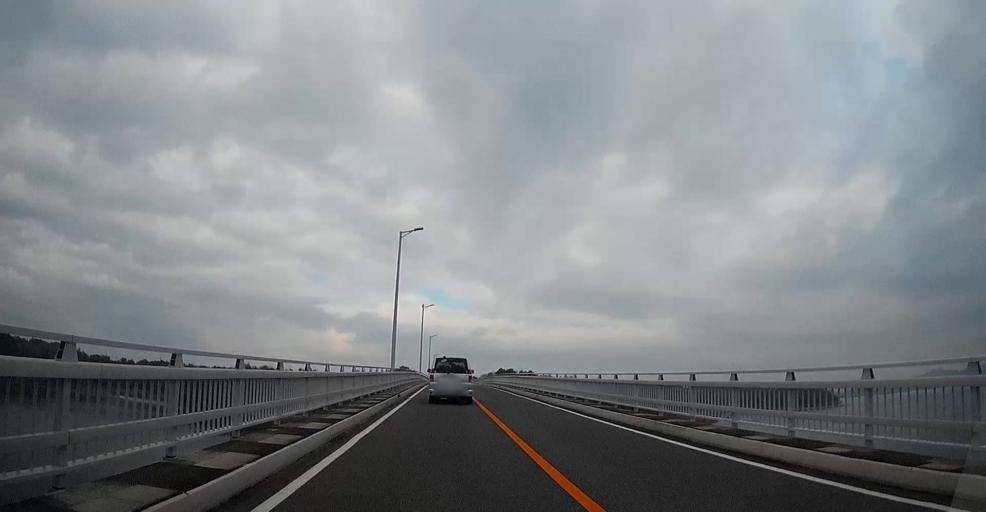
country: JP
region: Kumamoto
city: Yatsushiro
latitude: 32.5365
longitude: 130.4228
